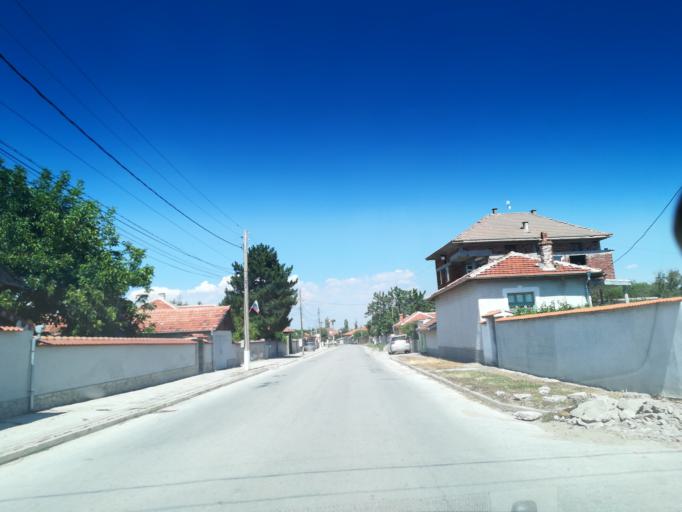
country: BG
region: Plovdiv
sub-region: Obshtina Sadovo
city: Sadovo
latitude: 42.0277
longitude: 25.1117
